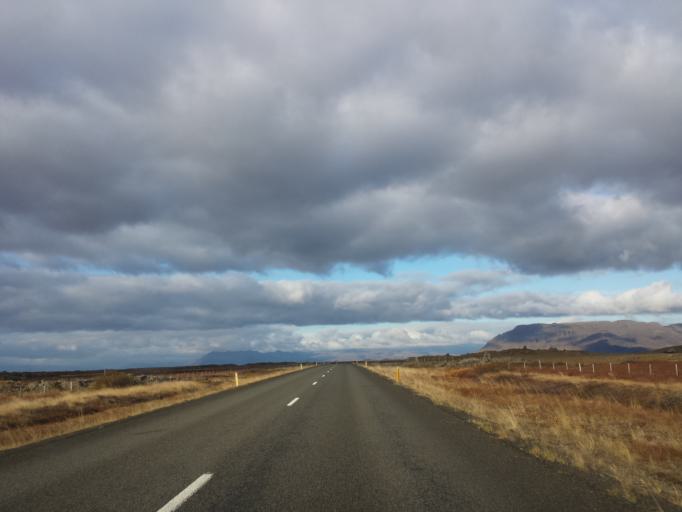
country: IS
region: West
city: Borgarnes
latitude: 64.6805
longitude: -22.0805
